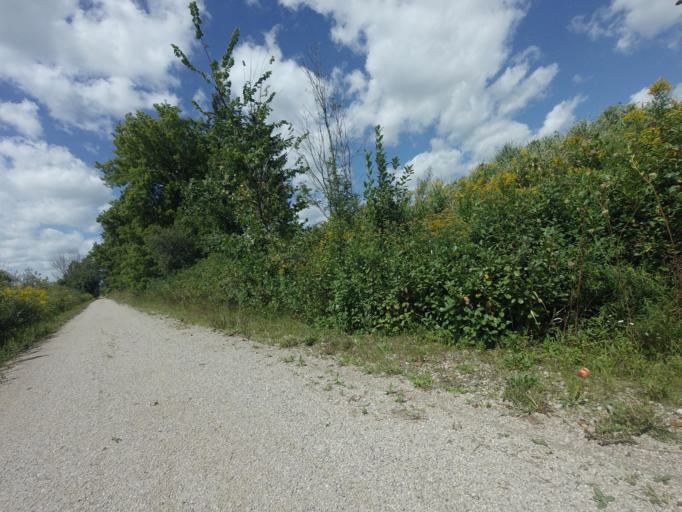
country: CA
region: Ontario
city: Huron East
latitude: 43.6279
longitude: -81.1726
